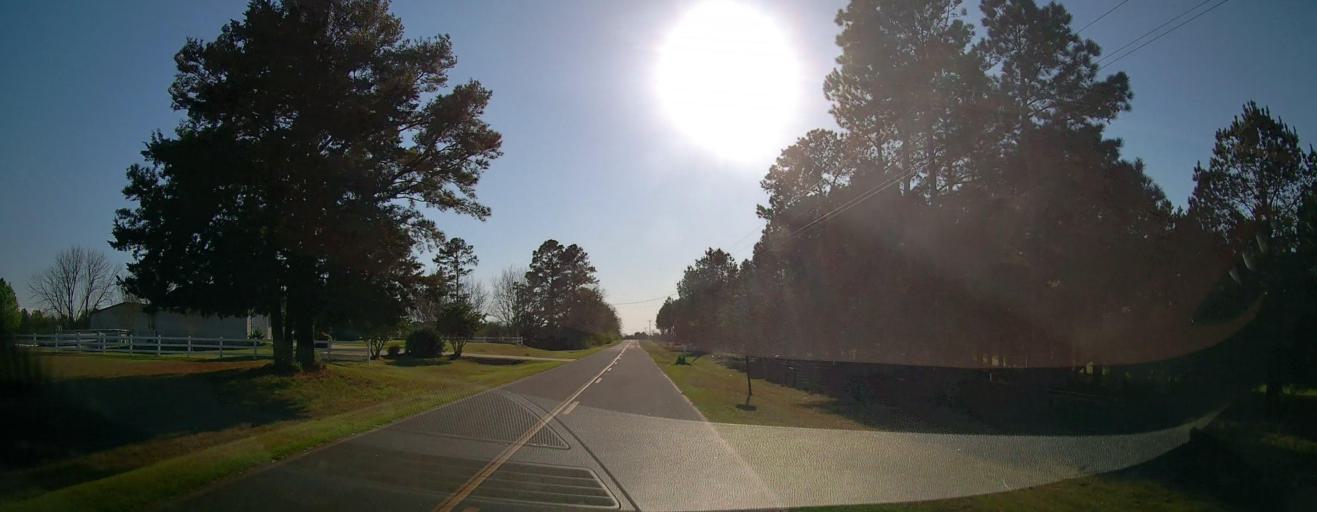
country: US
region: Georgia
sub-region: Pulaski County
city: Hawkinsville
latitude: 32.3260
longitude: -83.5624
